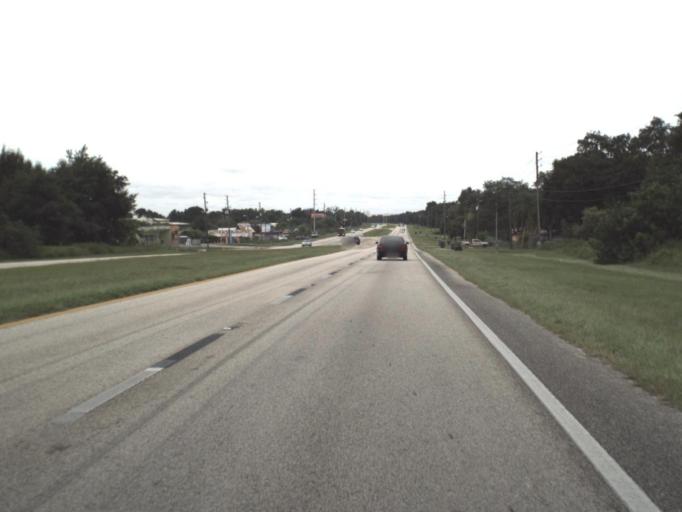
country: US
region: Florida
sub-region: Polk County
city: Eagle Lake
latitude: 27.9437
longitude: -81.7991
